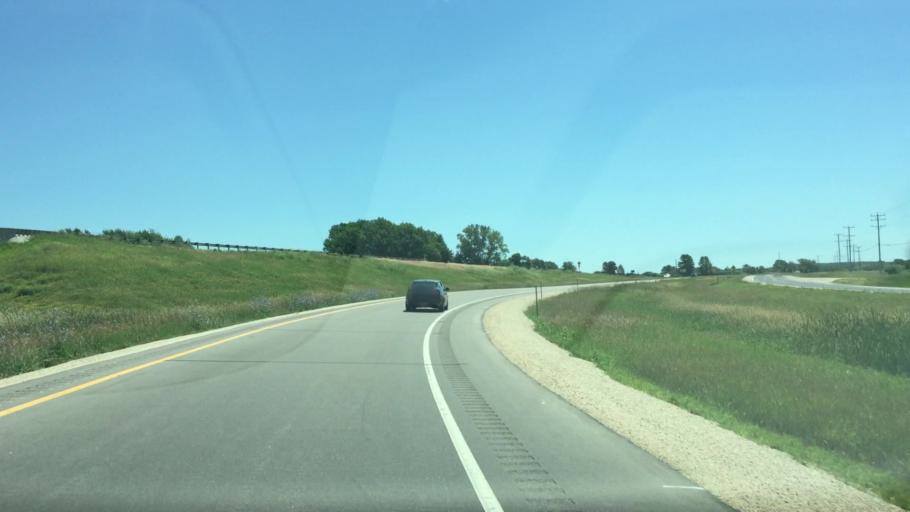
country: US
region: Wisconsin
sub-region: Outagamie County
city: Combined Locks
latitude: 44.2071
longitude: -88.3346
